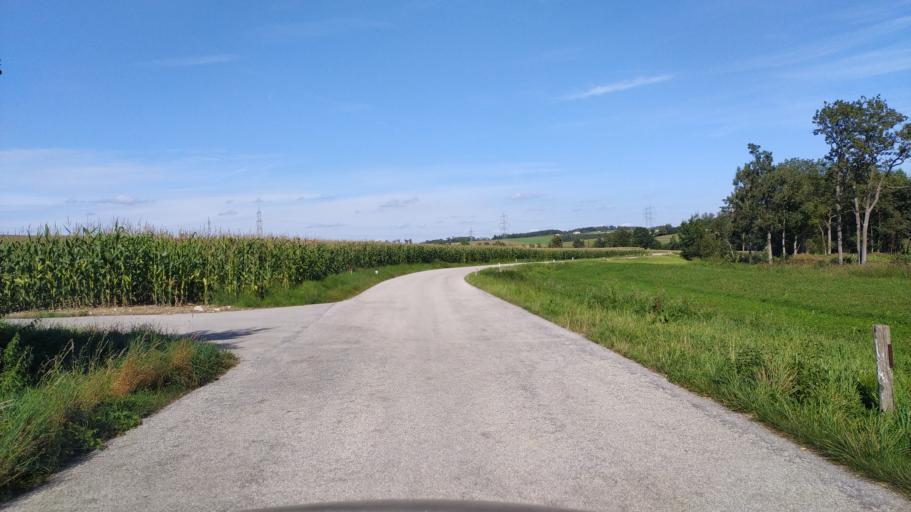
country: AT
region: Lower Austria
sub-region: Politischer Bezirk Amstetten
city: Strengberg
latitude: 48.1273
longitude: 14.6682
